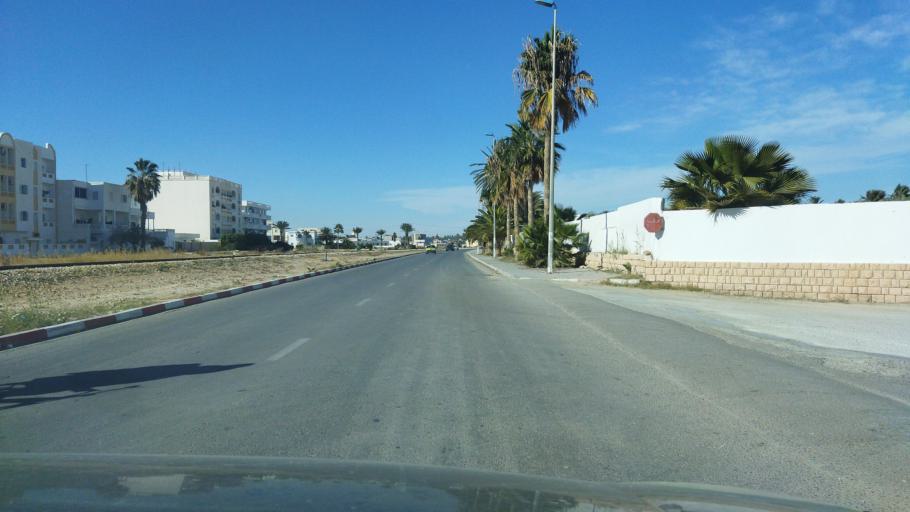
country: TN
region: Qabis
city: Gabes
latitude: 33.8889
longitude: 10.1152
